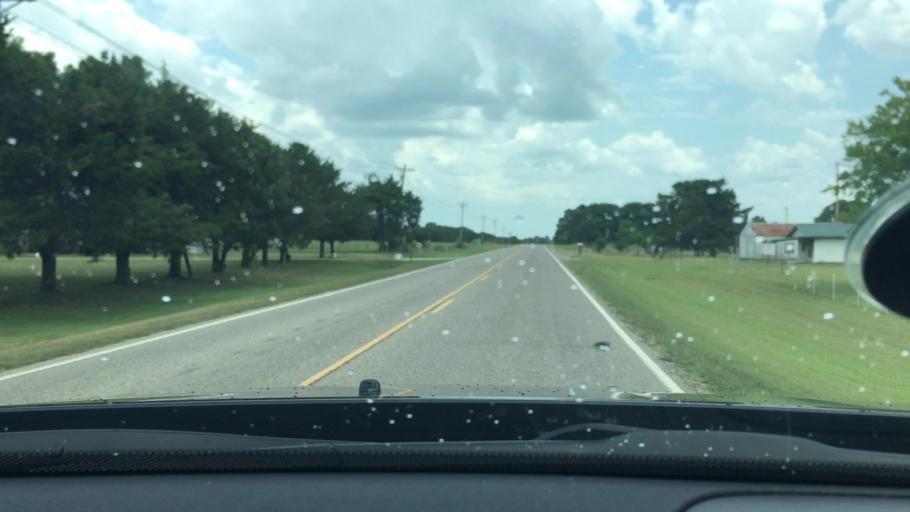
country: US
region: Oklahoma
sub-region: Love County
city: Marietta
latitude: 33.9553
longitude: -97.0302
